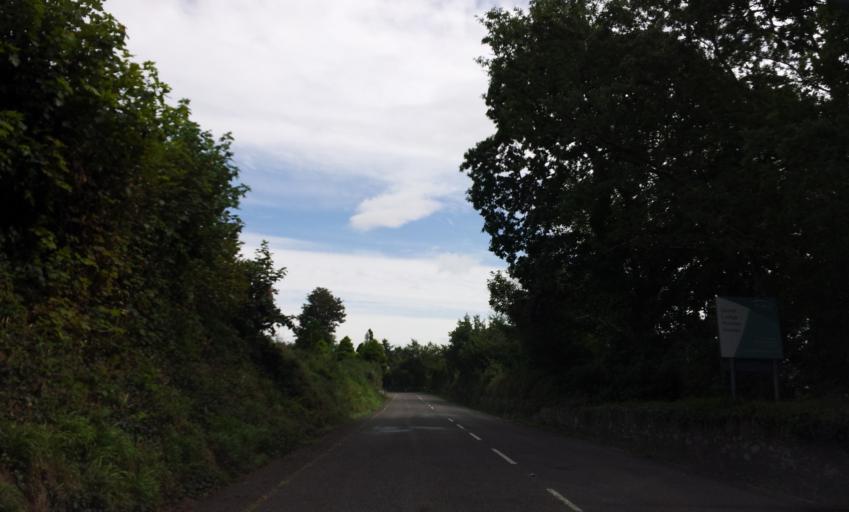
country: IE
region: Munster
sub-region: Ciarrai
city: Killorglin
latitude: 52.1025
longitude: -9.7746
